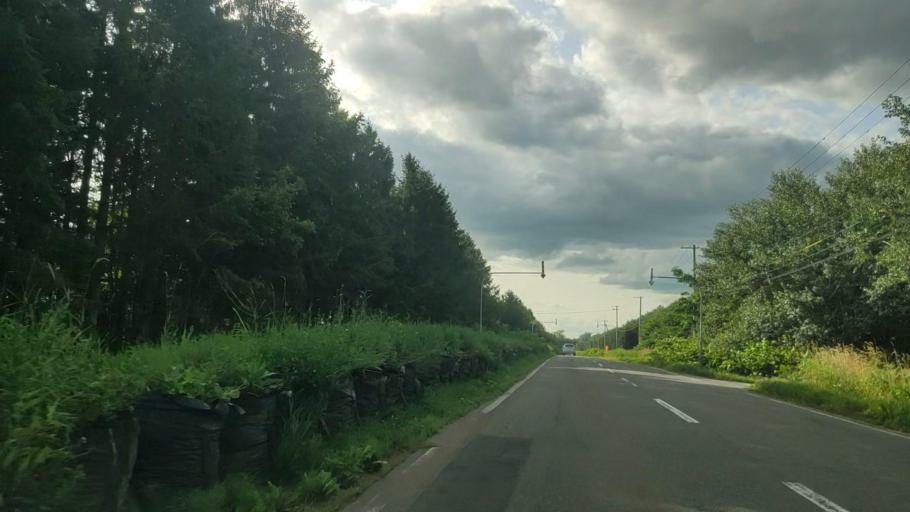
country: JP
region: Hokkaido
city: Makubetsu
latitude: 44.9007
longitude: 141.9113
